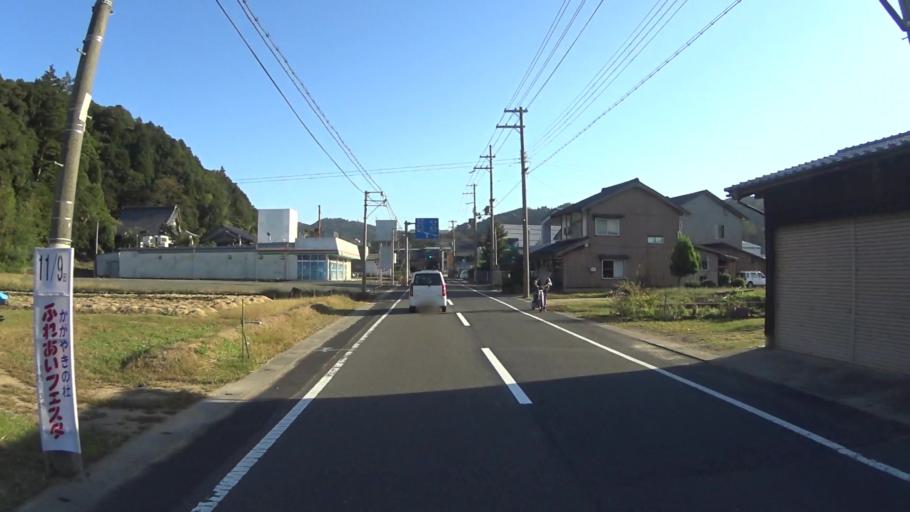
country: JP
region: Hyogo
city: Toyooka
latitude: 35.6040
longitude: 134.9018
